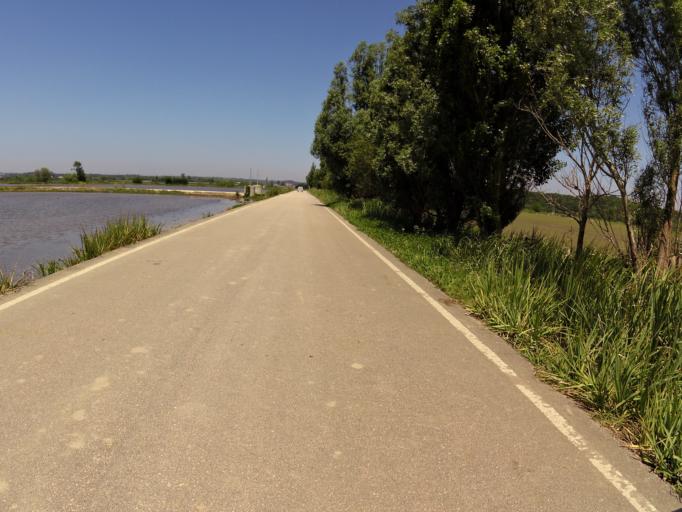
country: PT
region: Coimbra
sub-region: Montemor-O-Velho
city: Montemor-o-Velho
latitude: 40.1631
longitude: -8.7167
